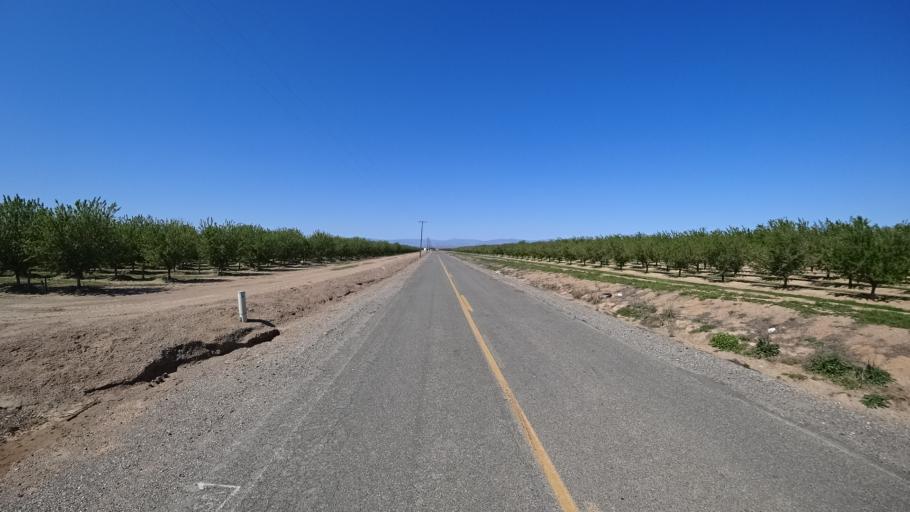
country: US
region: California
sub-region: Glenn County
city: Orland
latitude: 39.6972
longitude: -122.2340
